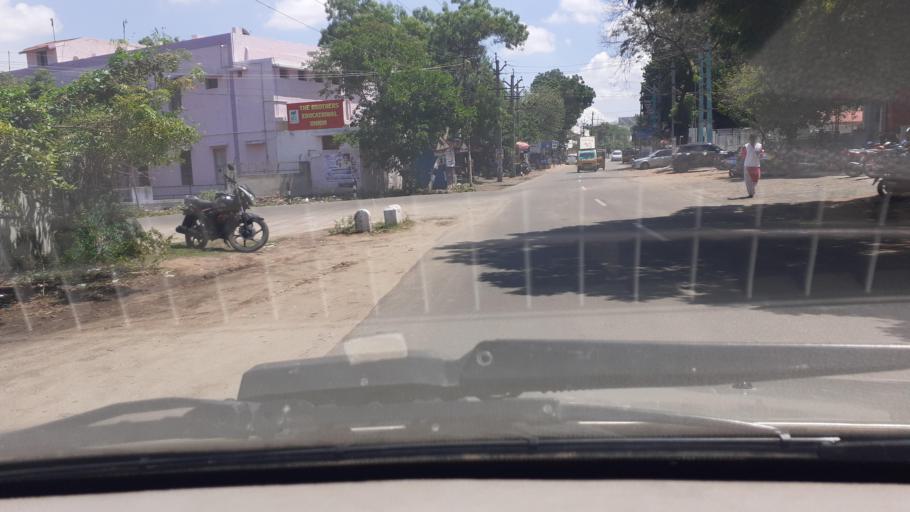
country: IN
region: Tamil Nadu
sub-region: Tirunelveli Kattabo
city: Tirunelveli
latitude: 8.7187
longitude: 77.7414
